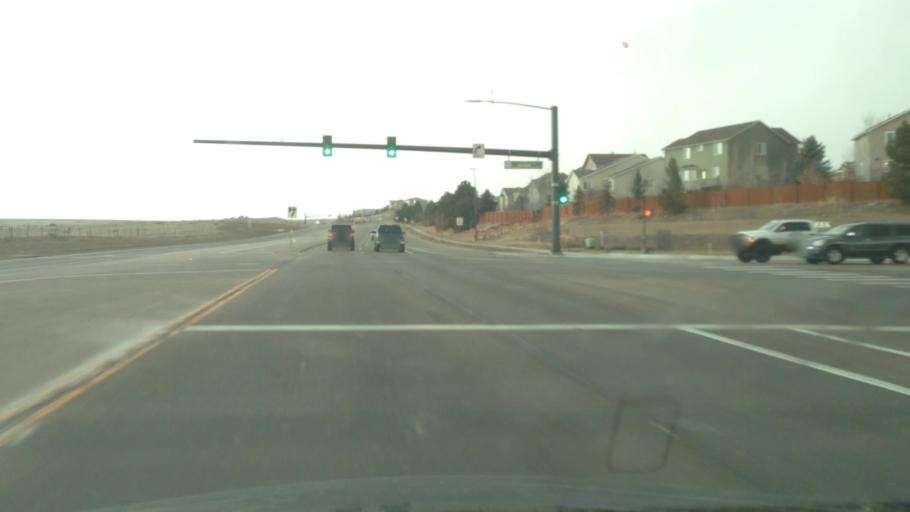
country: US
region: Colorado
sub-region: Douglas County
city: Stonegate
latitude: 39.4930
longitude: -104.7933
